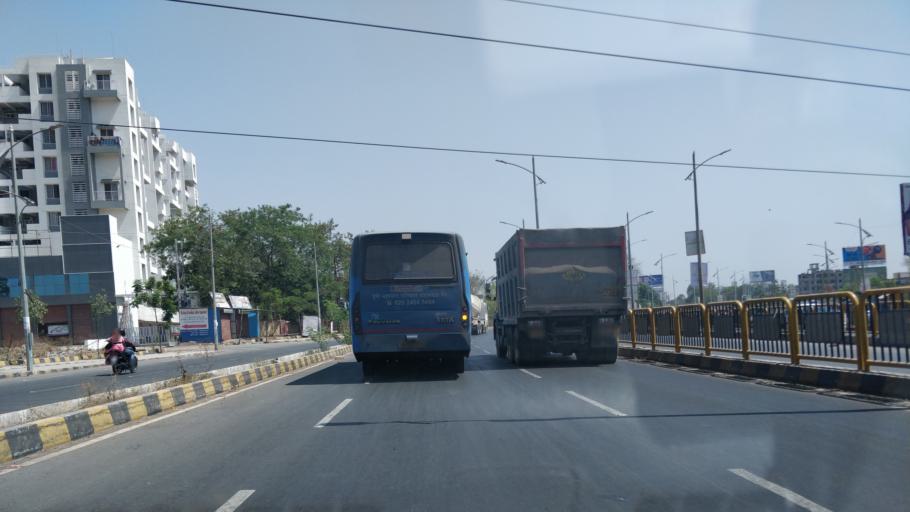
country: IN
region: Maharashtra
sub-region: Pune Division
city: Alandi
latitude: 18.6639
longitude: 73.8870
